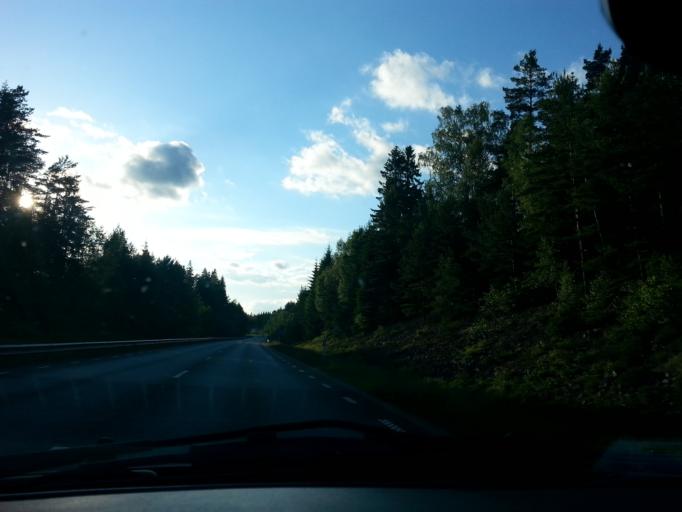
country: SE
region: Joenkoeping
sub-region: Gislaveds Kommun
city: Gislaved
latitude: 57.3329
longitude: 13.5210
